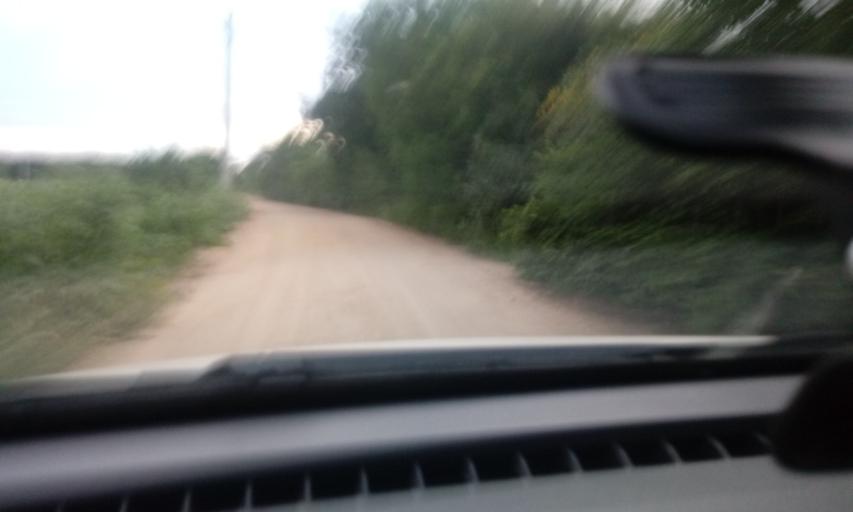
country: BR
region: Bahia
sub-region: Riacho De Santana
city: Riacho de Santana
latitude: -13.8031
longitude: -42.7539
